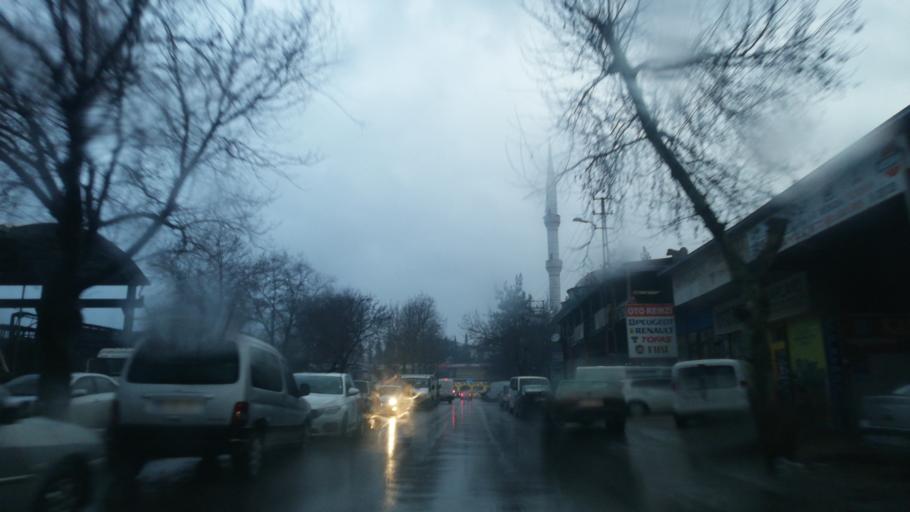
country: TR
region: Kahramanmaras
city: Kahramanmaras
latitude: 37.5643
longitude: 36.9543
